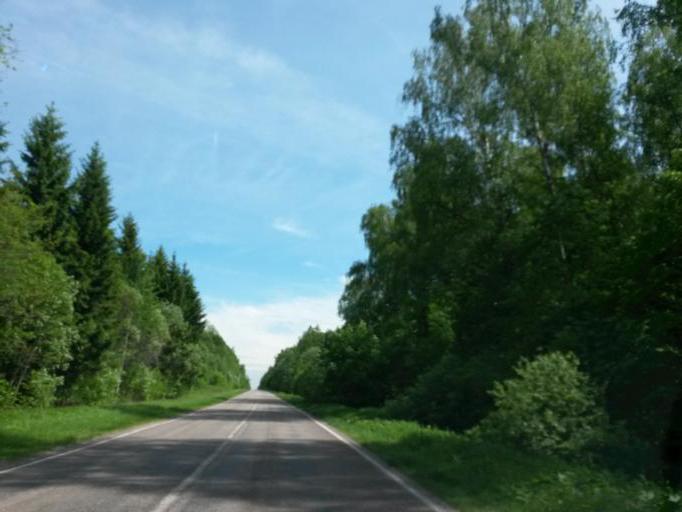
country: RU
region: Moskovskaya
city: Melikhovo
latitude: 55.2247
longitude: 37.6576
